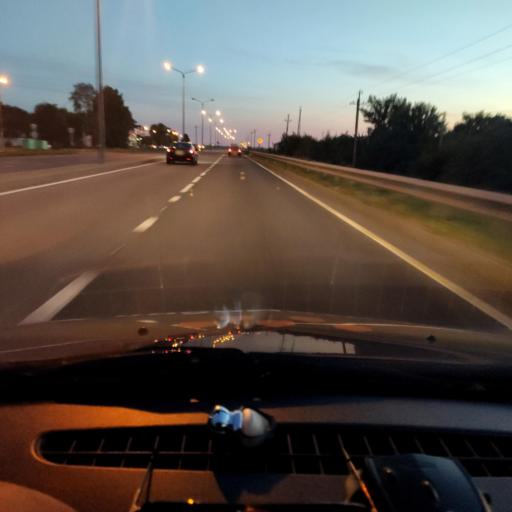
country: RU
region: Belgorod
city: Gubkin
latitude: 51.2621
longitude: 37.5388
